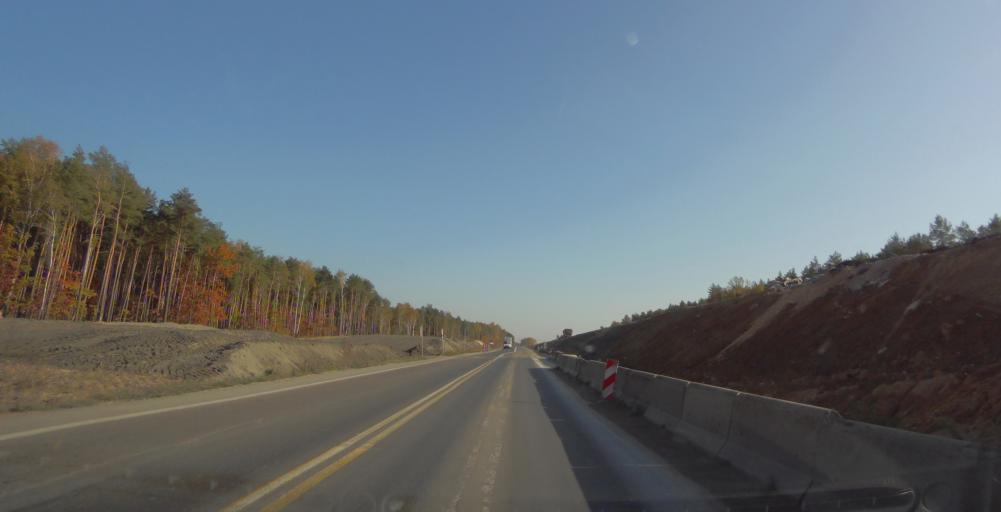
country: PL
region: Masovian Voivodeship
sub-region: Powiat otwocki
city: Celestynow
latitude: 52.0846
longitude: 21.4316
